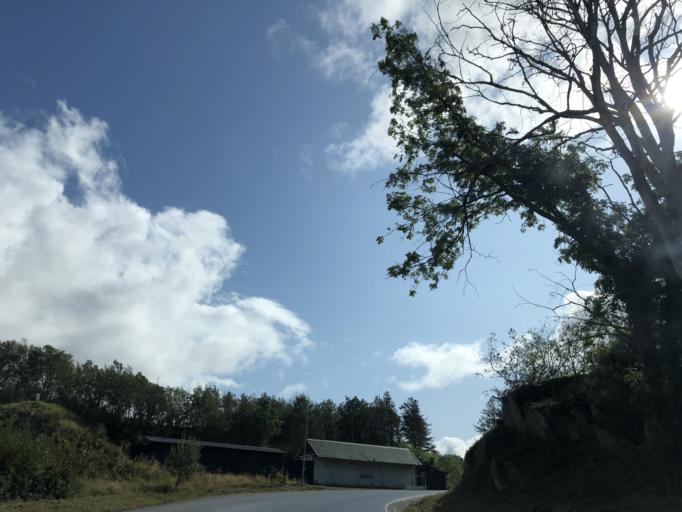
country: SE
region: Vaestra Goetaland
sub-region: Goteborg
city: Majorna
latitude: 57.7149
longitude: 11.8511
